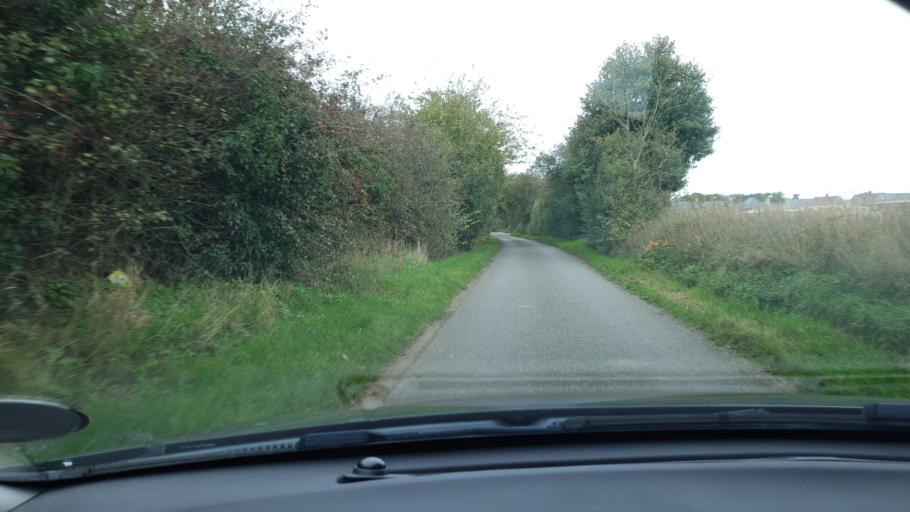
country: GB
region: England
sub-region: Essex
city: Manningtree
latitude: 51.9341
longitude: 1.0520
